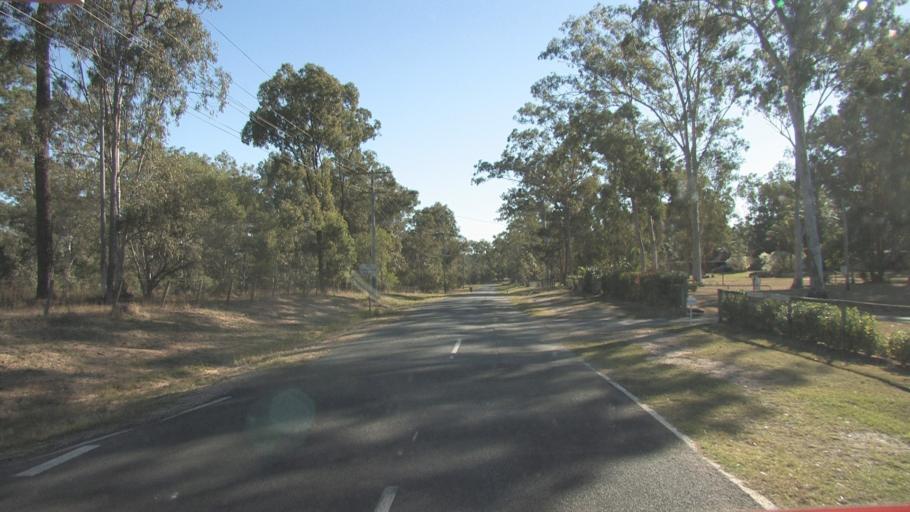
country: AU
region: Queensland
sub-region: Logan
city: Park Ridge South
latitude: -27.7357
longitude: 153.0179
